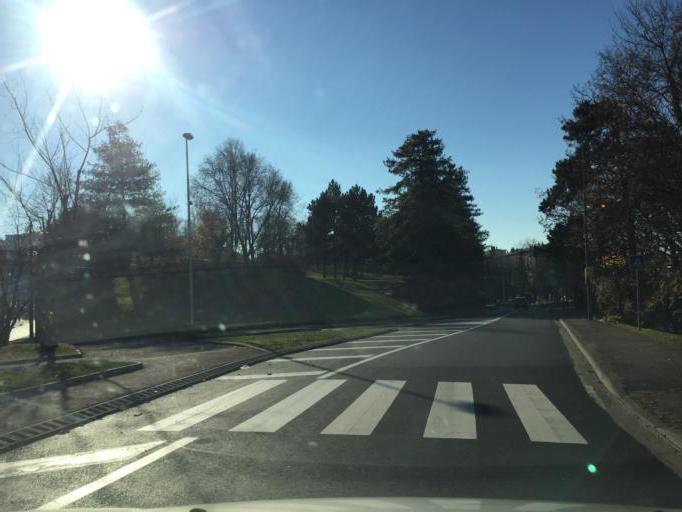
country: FR
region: Rhone-Alpes
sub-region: Departement du Rhone
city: Caluire-et-Cuire
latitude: 45.7998
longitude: 4.8512
